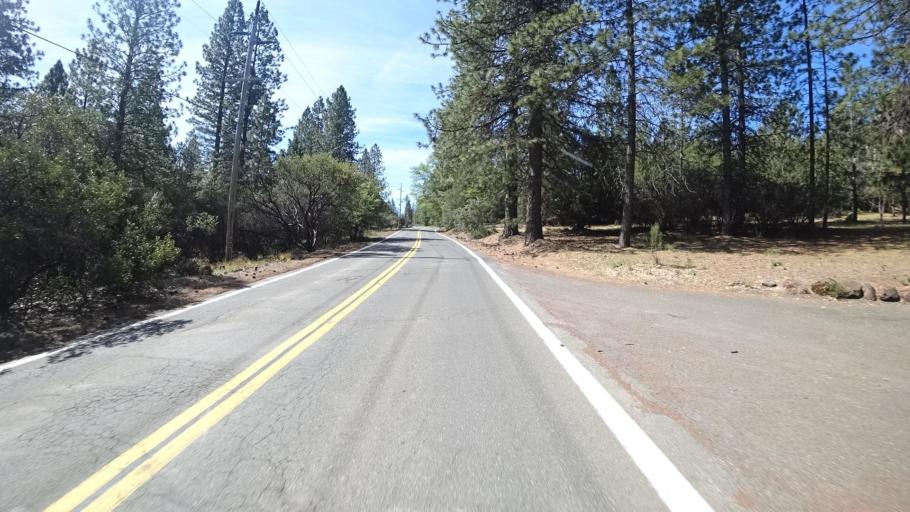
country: US
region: California
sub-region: Lake County
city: Cobb
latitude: 38.8882
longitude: -122.7859
